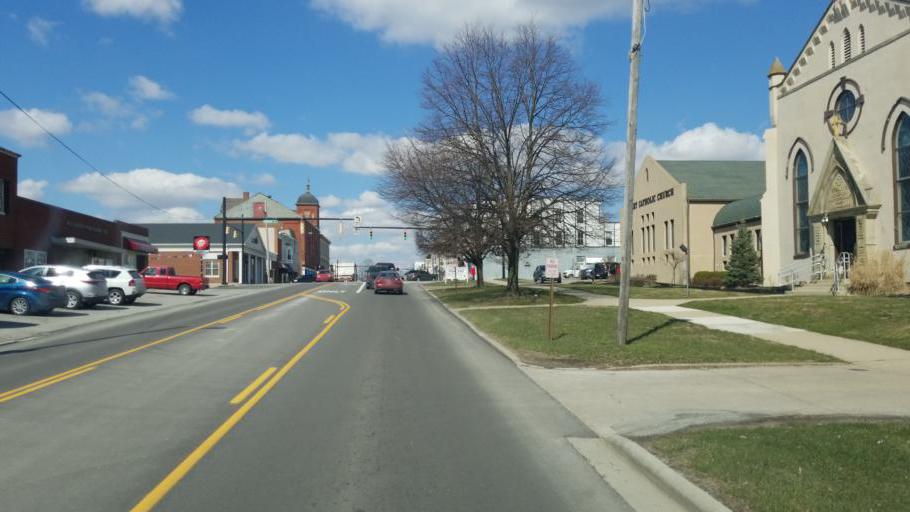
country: US
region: Ohio
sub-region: Highland County
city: Hillsboro
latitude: 39.2001
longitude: -83.6120
